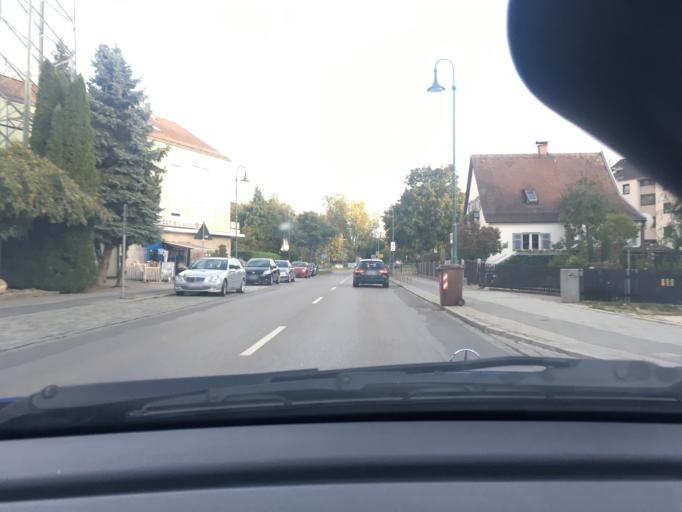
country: DE
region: Bavaria
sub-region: Swabia
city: Stadtbergen
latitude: 48.3875
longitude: 10.8409
